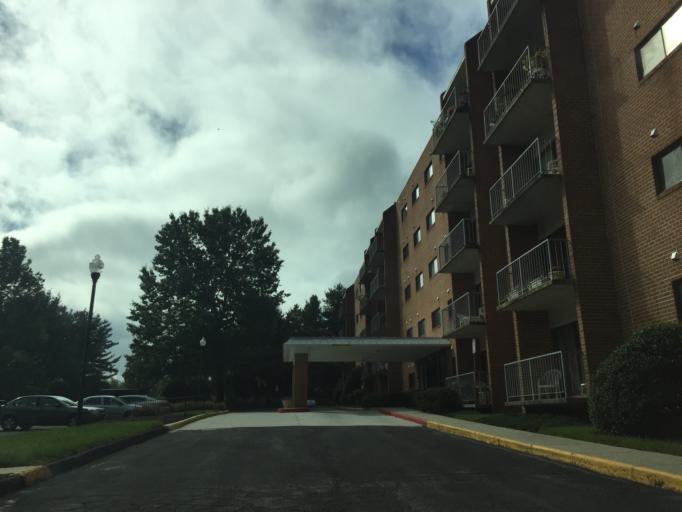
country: US
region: Maryland
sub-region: Baltimore County
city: Mays Chapel
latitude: 39.3887
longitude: -76.6691
